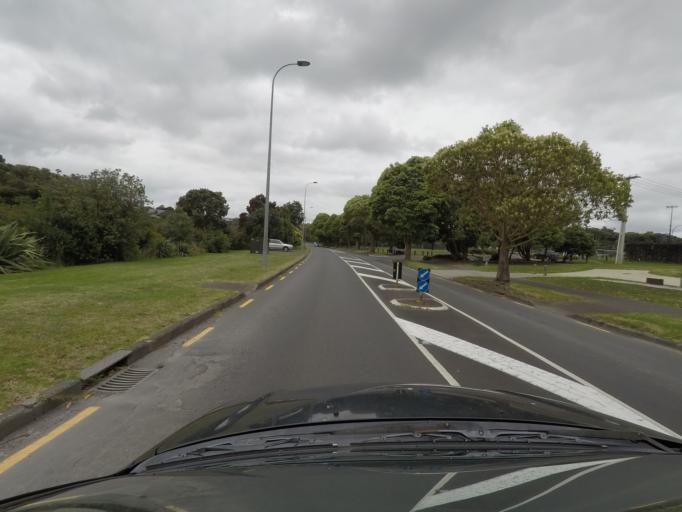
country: NZ
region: Auckland
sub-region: Auckland
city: Rosebank
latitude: -36.8587
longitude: 174.7156
